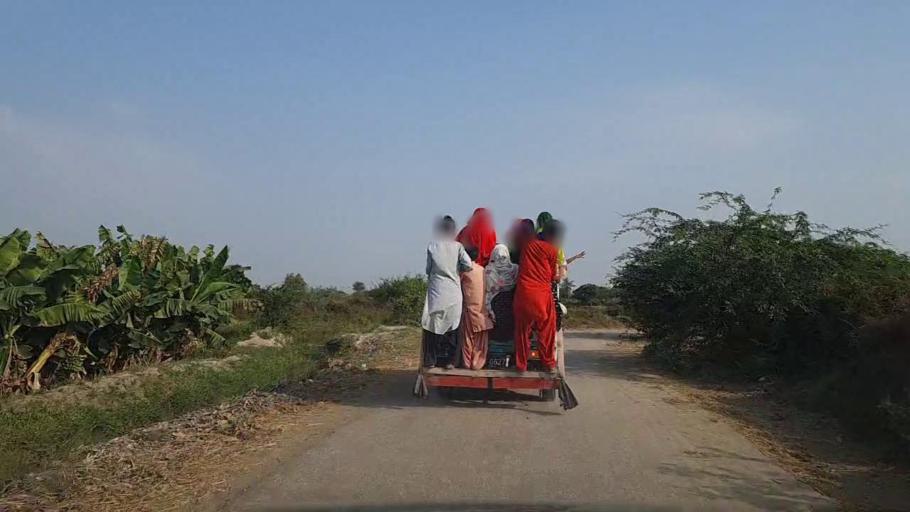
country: PK
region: Sindh
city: Thatta
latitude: 24.6460
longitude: 67.9307
